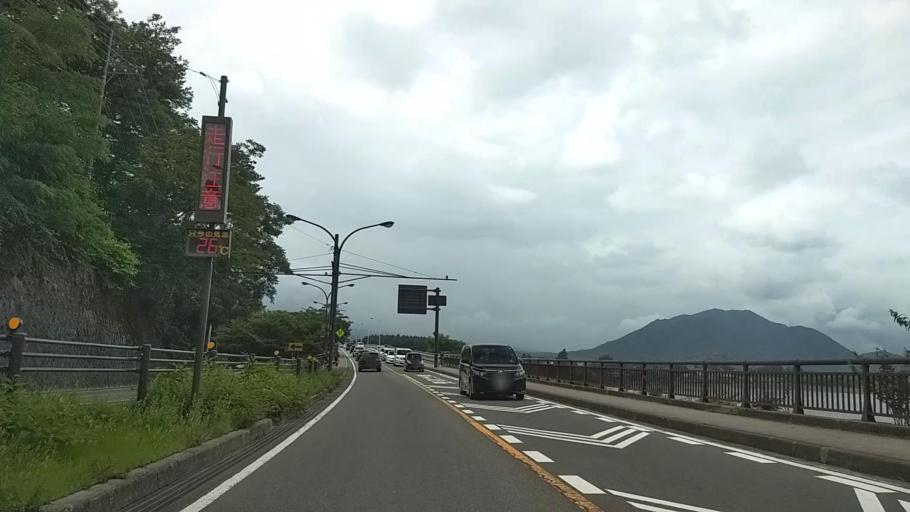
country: JP
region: Yamanashi
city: Fujikawaguchiko
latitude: 35.5144
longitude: 138.7670
